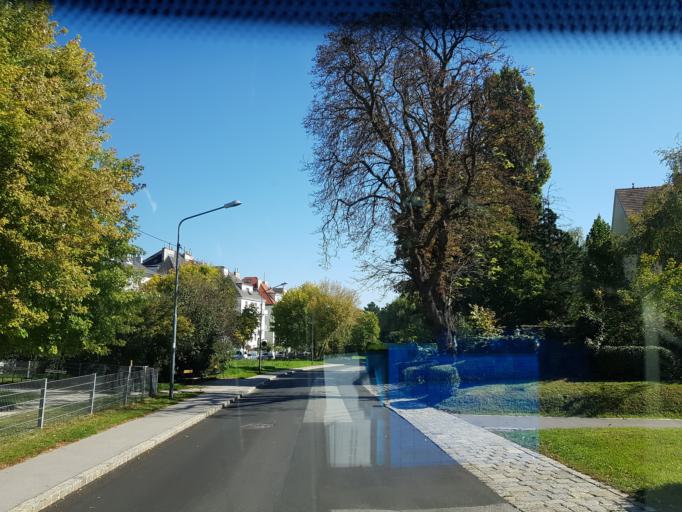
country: AT
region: Lower Austria
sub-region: Politischer Bezirk Korneuburg
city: Langenzersdorf
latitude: 48.2506
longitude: 16.3376
